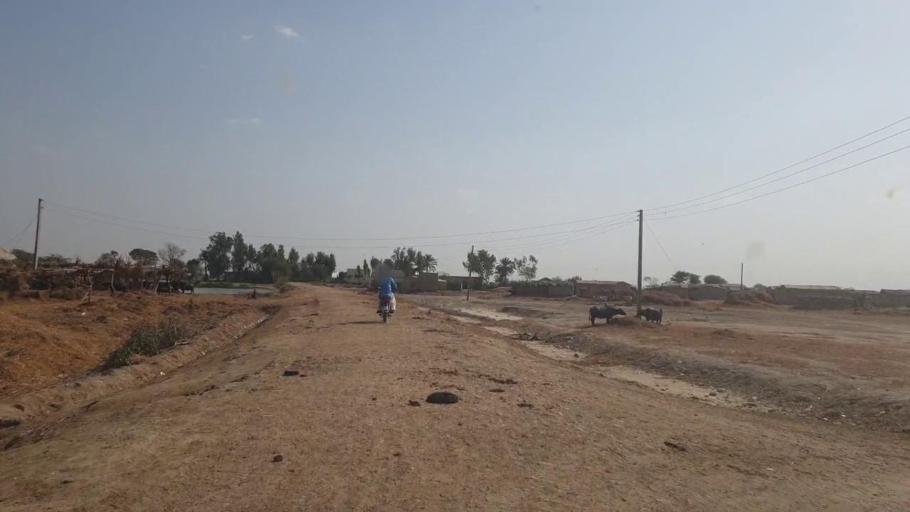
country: PK
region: Sindh
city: Jati
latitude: 24.5144
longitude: 68.5253
